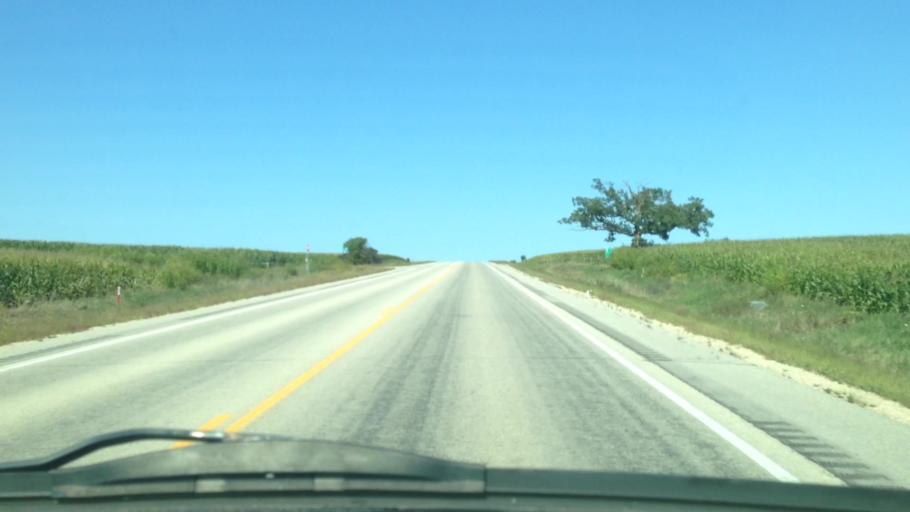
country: US
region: Minnesota
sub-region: Fillmore County
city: Rushford
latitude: 43.8536
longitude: -91.7473
